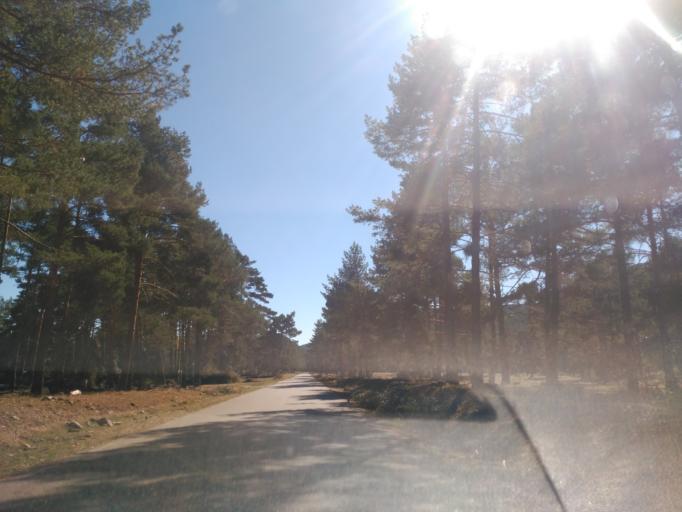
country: ES
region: Castille and Leon
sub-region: Provincia de Soria
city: Vinuesa
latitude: 41.9386
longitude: -2.7789
